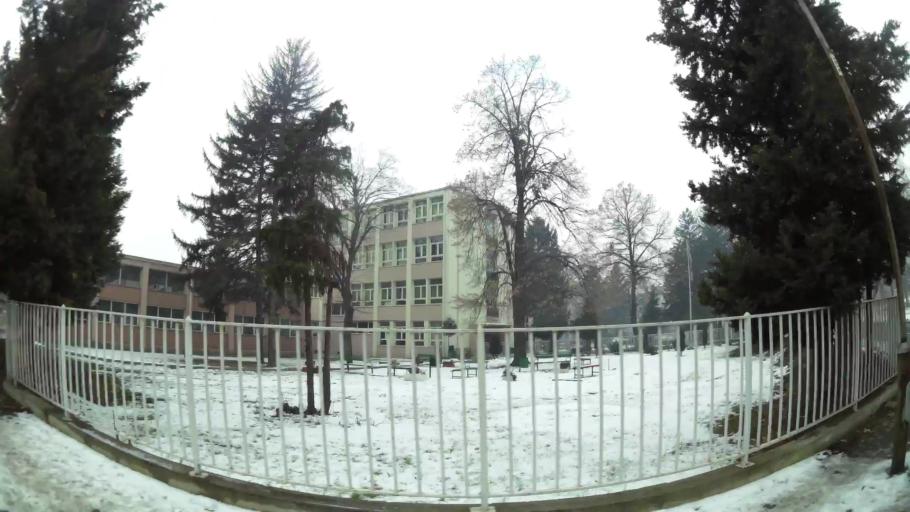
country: MK
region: Cair
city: Cair
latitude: 42.0069
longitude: 21.4652
